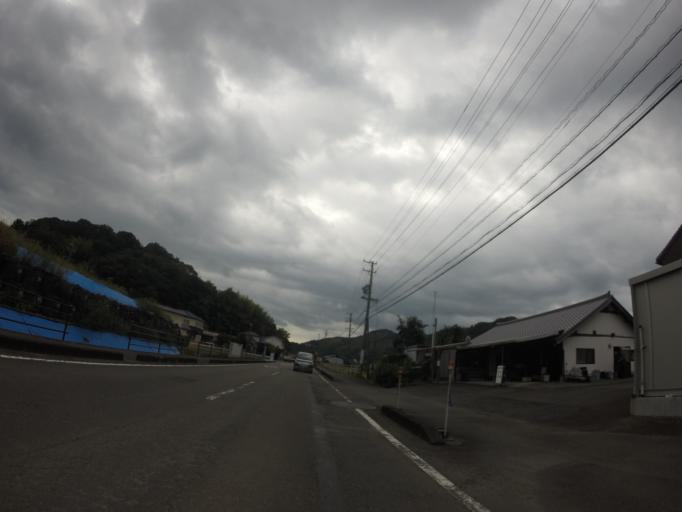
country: JP
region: Shizuoka
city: Fujieda
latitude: 34.9075
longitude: 138.2624
